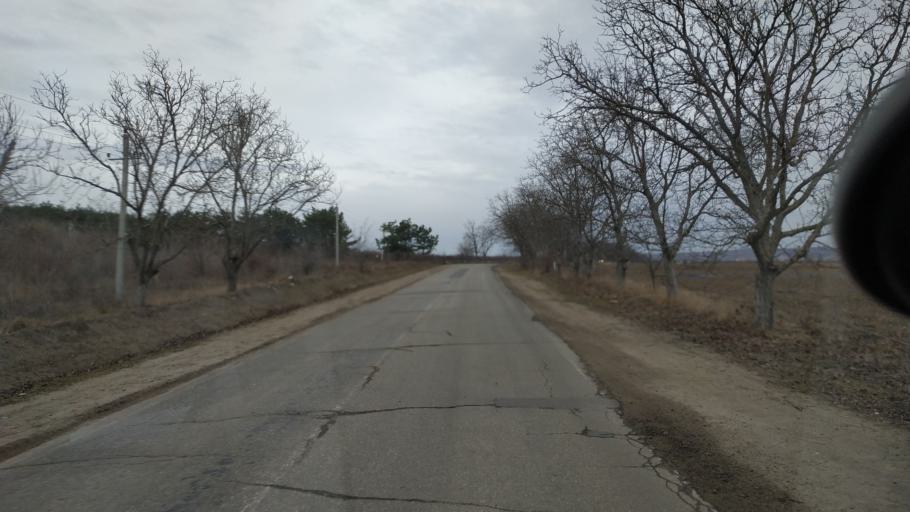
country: MD
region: Criuleni
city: Criuleni
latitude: 47.2412
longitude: 29.1477
